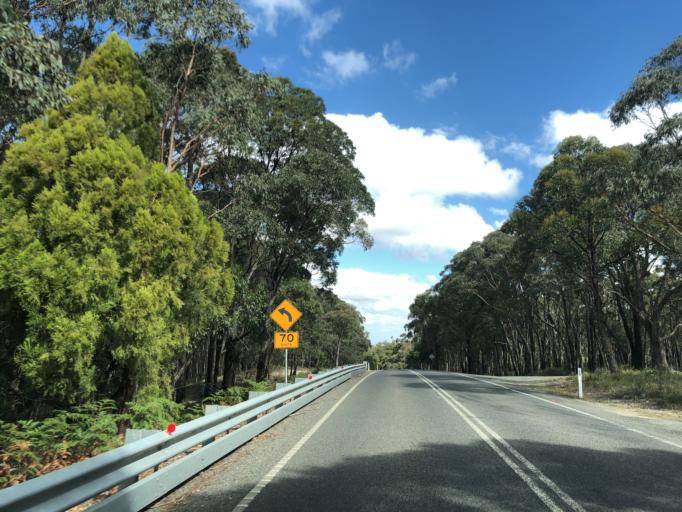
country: AU
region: Victoria
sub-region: Moorabool
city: Bacchus Marsh
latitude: -37.5066
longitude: 144.3108
